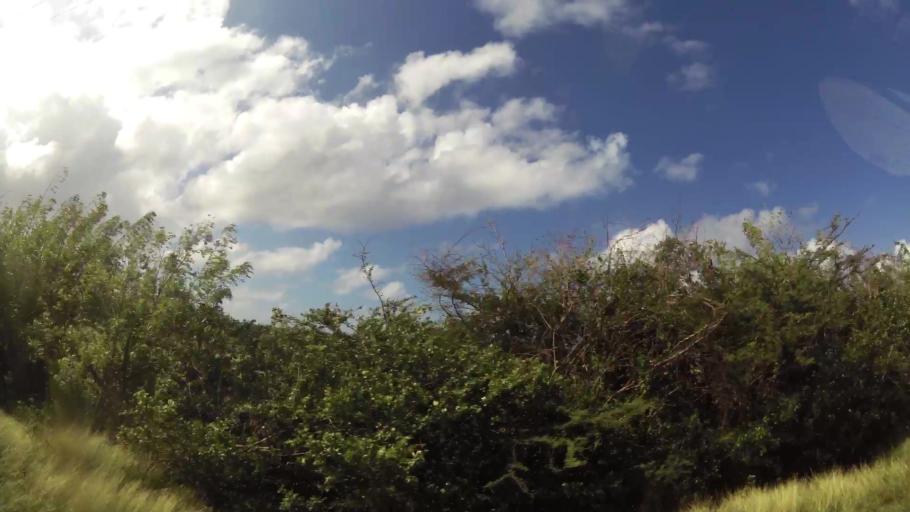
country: MQ
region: Martinique
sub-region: Martinique
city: Le Marin
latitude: 14.4085
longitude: -60.8772
